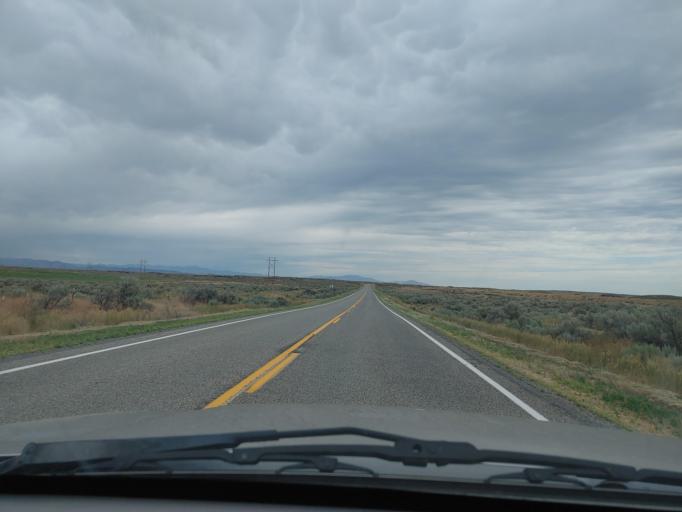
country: US
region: Idaho
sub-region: Lincoln County
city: Shoshone
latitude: 43.0857
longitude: -114.0968
